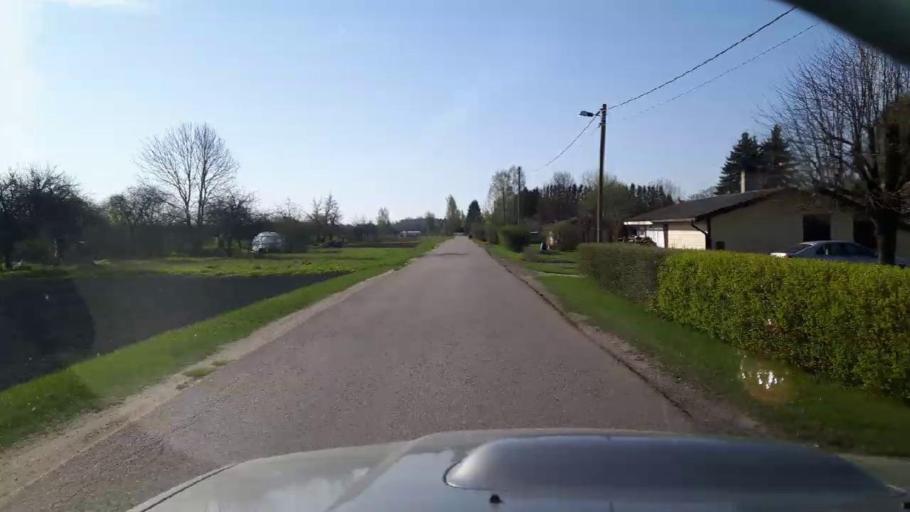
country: EE
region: Paernumaa
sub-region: Tootsi vald
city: Tootsi
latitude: 58.4914
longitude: 24.9054
